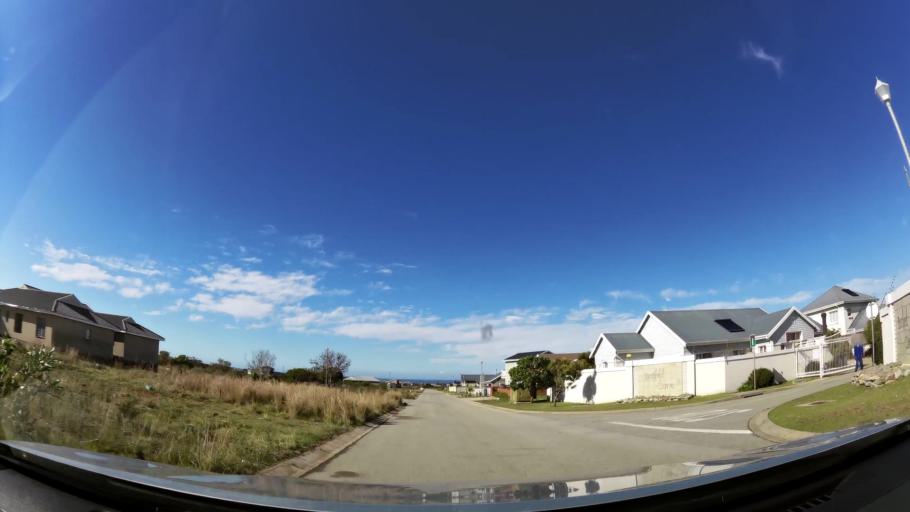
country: ZA
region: Eastern Cape
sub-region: Cacadu District Municipality
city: Jeffrey's Bay
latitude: -34.0347
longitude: 24.9038
